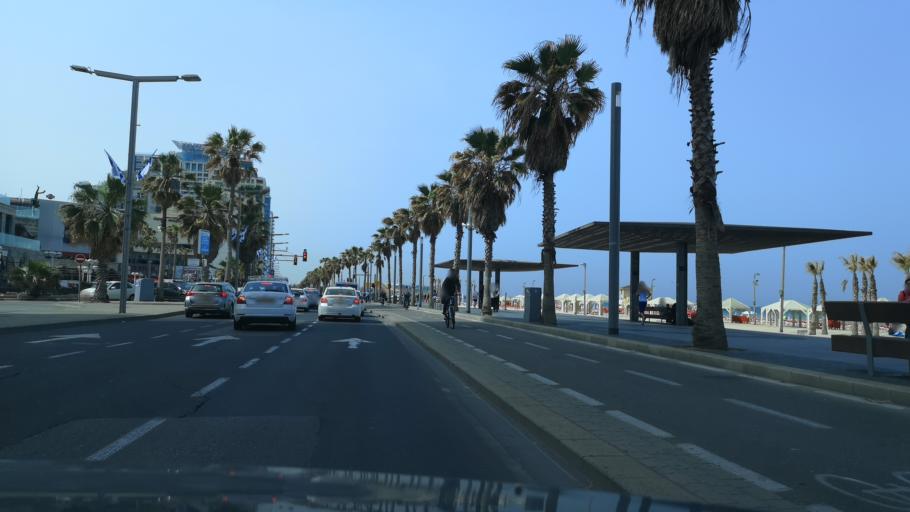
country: IL
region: Tel Aviv
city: Tel Aviv
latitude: 32.0749
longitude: 34.7654
